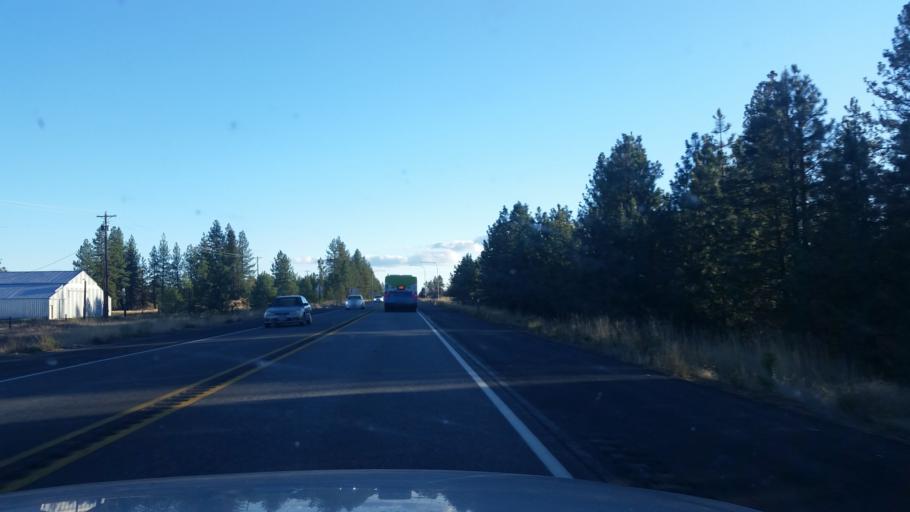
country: US
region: Washington
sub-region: Spokane County
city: Cheney
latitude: 47.5161
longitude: -117.5646
